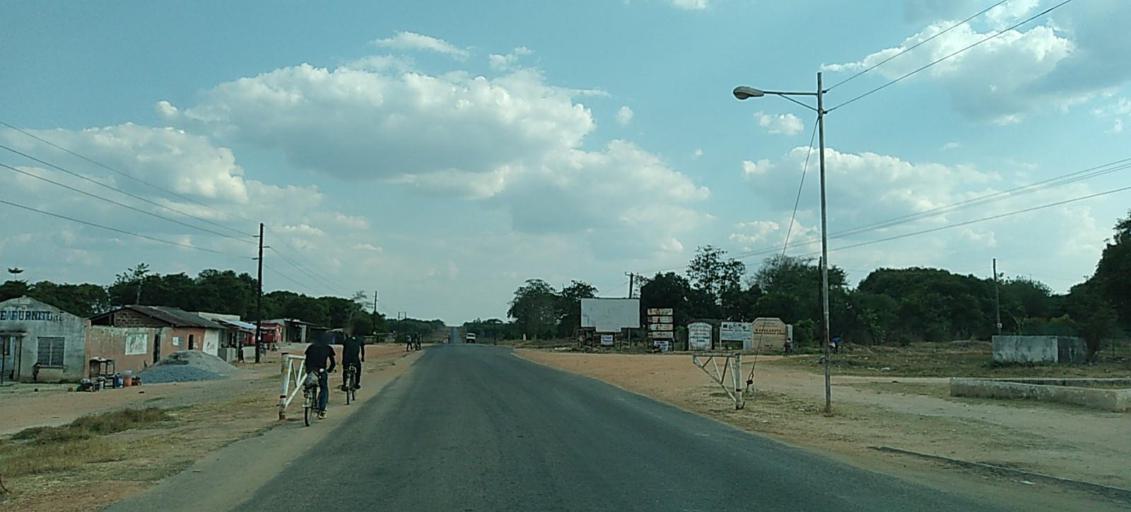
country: ZM
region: Copperbelt
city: Luanshya
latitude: -13.2610
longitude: 28.4063
